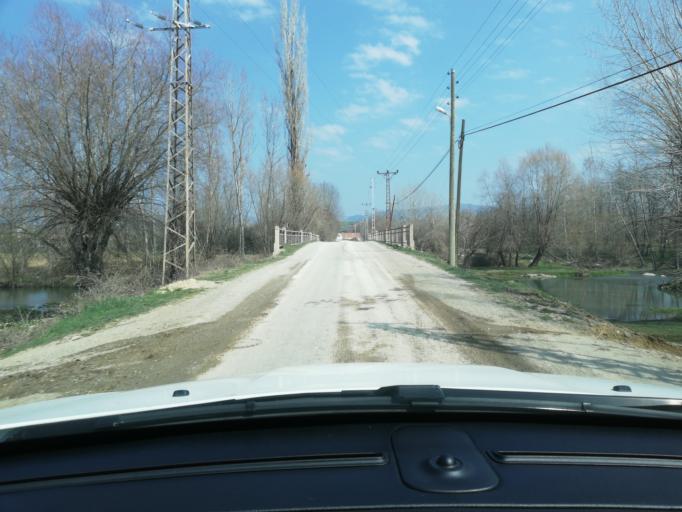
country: TR
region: Kastamonu
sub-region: Cide
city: Kastamonu
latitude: 41.4532
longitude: 33.7669
